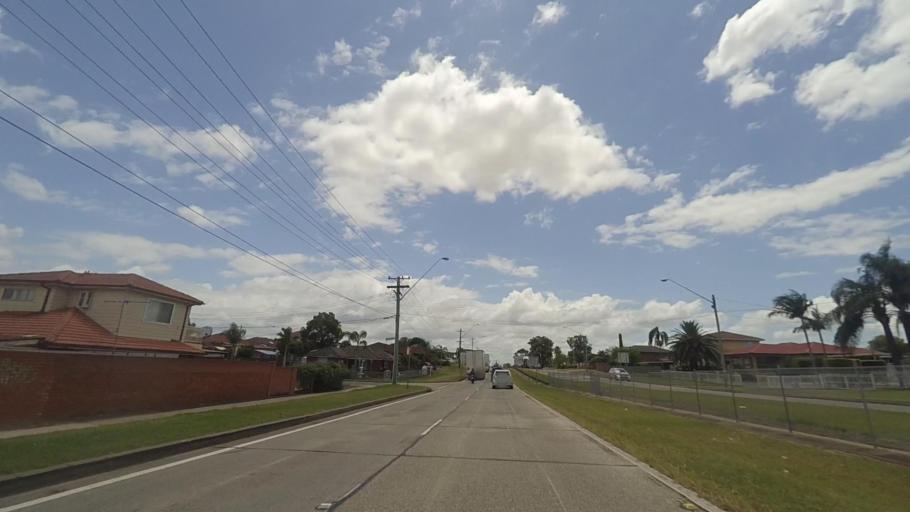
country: AU
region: New South Wales
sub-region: Fairfield
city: Fairfield Heights
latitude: -33.8668
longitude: 150.9257
